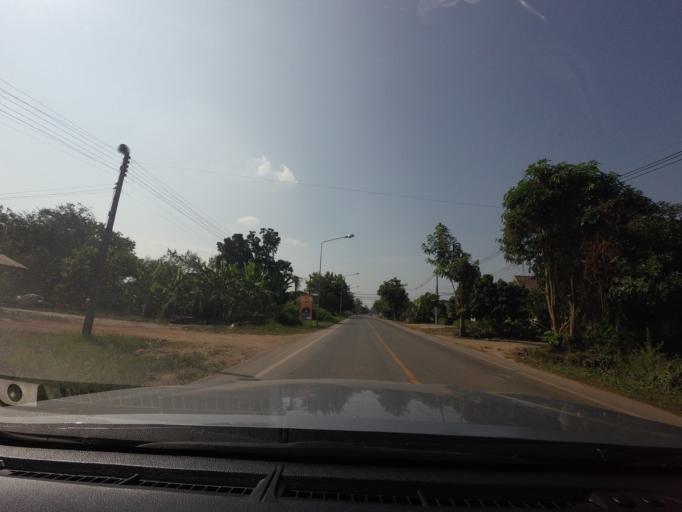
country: TH
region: Phitsanulok
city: Bang Rakam
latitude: 16.8089
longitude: 100.0186
